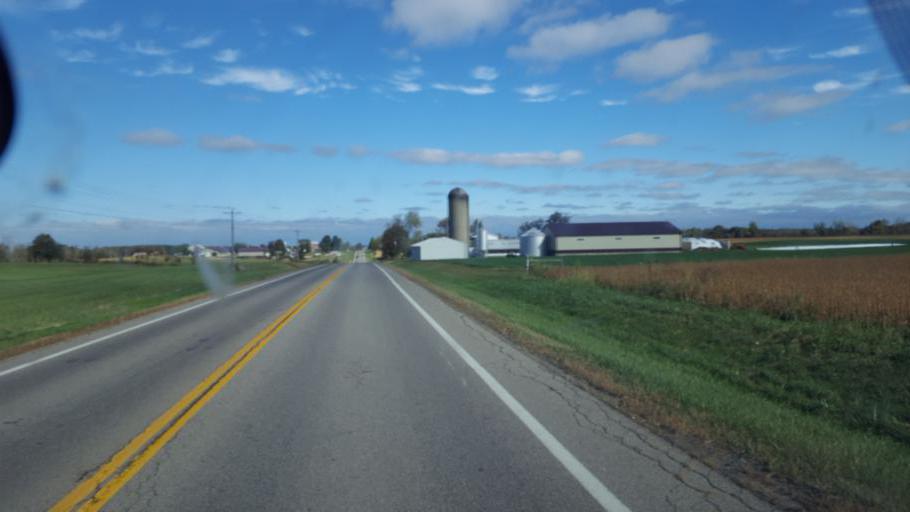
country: US
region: Ohio
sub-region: Huron County
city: Greenwich
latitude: 41.0026
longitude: -82.4839
